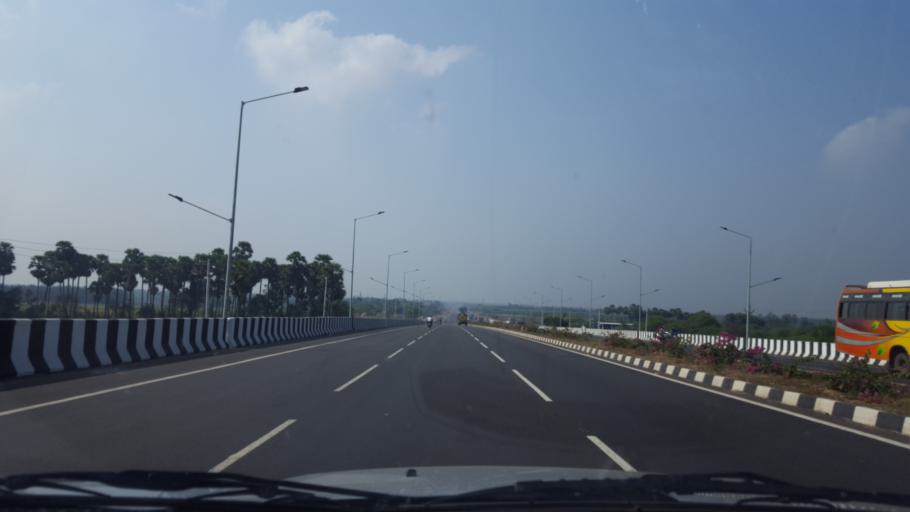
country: IN
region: Andhra Pradesh
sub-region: Vizianagaram District
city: Vizianagaram
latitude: 18.0491
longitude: 83.5143
